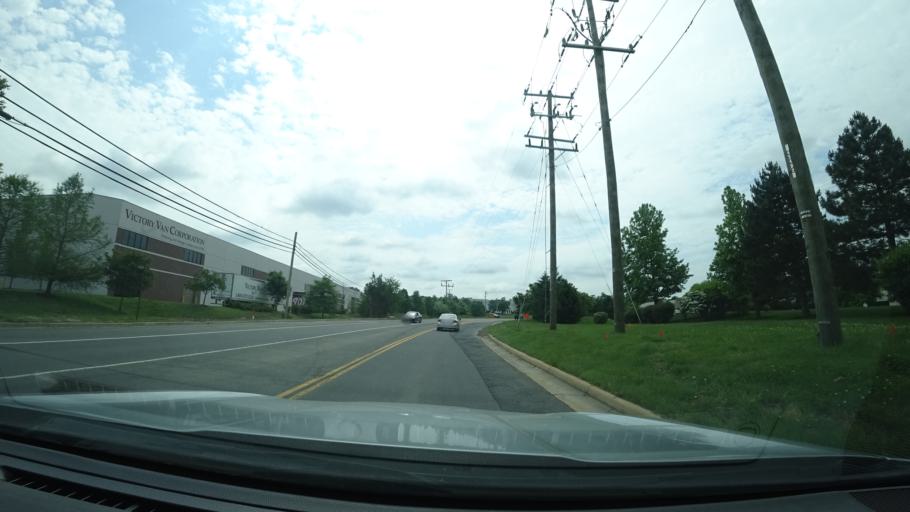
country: US
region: Virginia
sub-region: Loudoun County
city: Oak Grove
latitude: 38.9857
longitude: -77.4242
